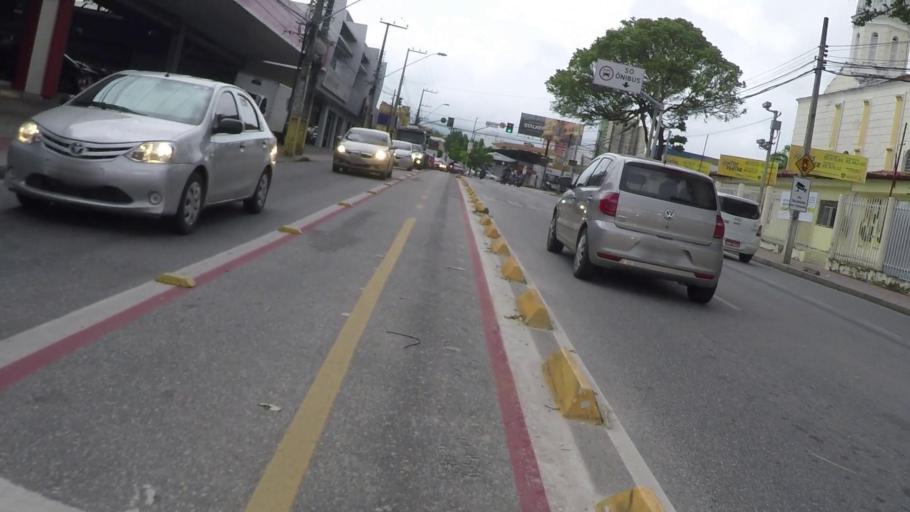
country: BR
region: Ceara
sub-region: Fortaleza
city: Fortaleza
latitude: -3.7386
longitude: -38.5243
